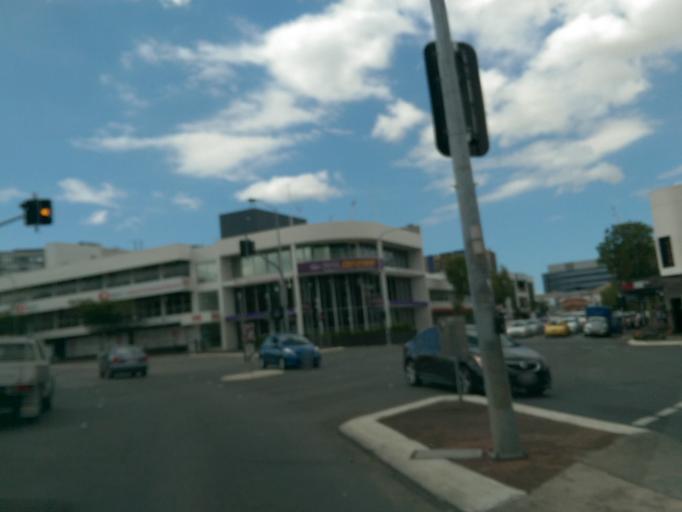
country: AU
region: Queensland
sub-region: Brisbane
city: Fortitude Valley
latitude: -27.4564
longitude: 153.0315
